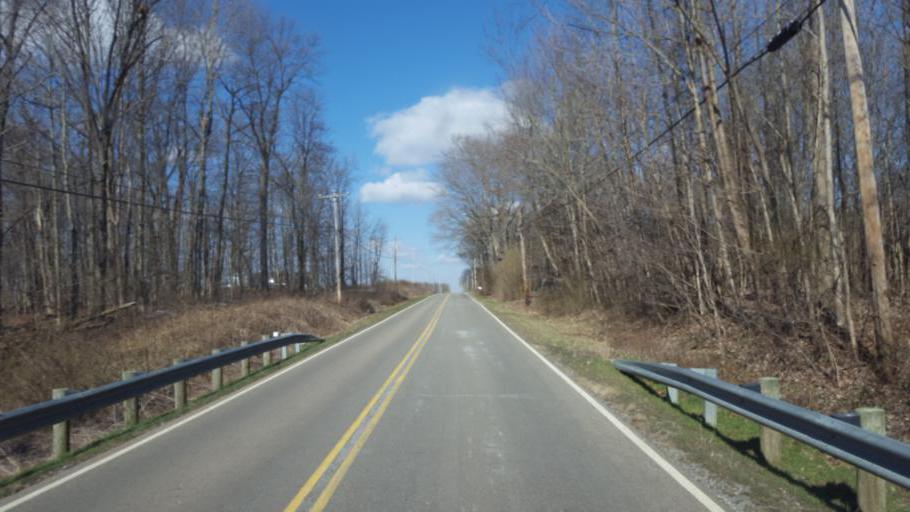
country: US
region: Ohio
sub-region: Licking County
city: Utica
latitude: 40.2347
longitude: -82.4713
